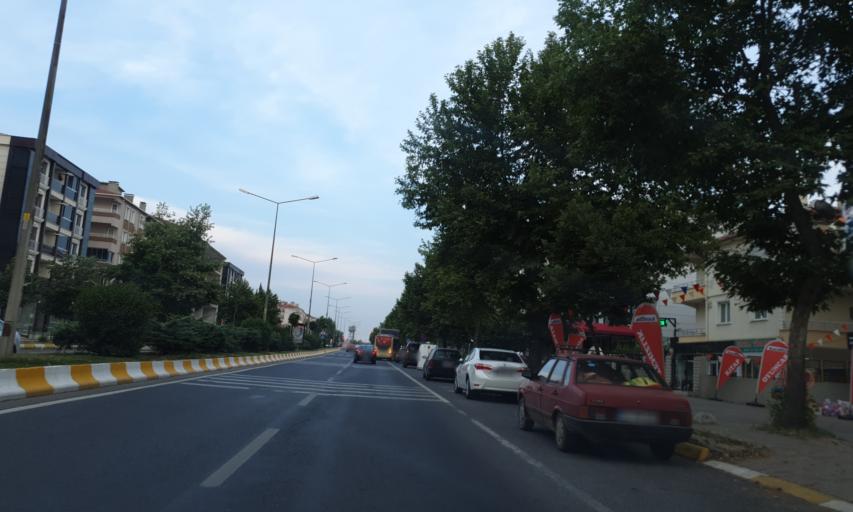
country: TR
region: Kirklareli
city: Luleburgaz
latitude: 41.4021
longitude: 27.3682
